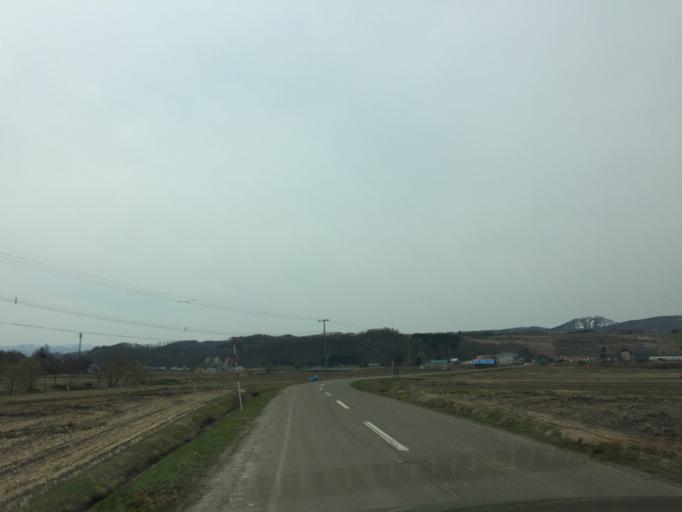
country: JP
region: Hokkaido
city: Ashibetsu
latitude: 43.6144
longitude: 142.2147
